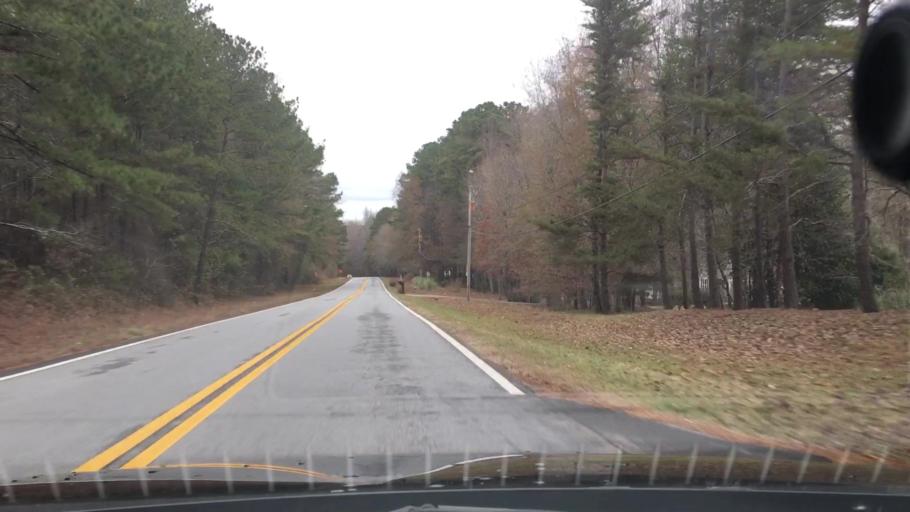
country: US
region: Georgia
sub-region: Coweta County
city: East Newnan
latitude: 33.4161
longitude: -84.7026
